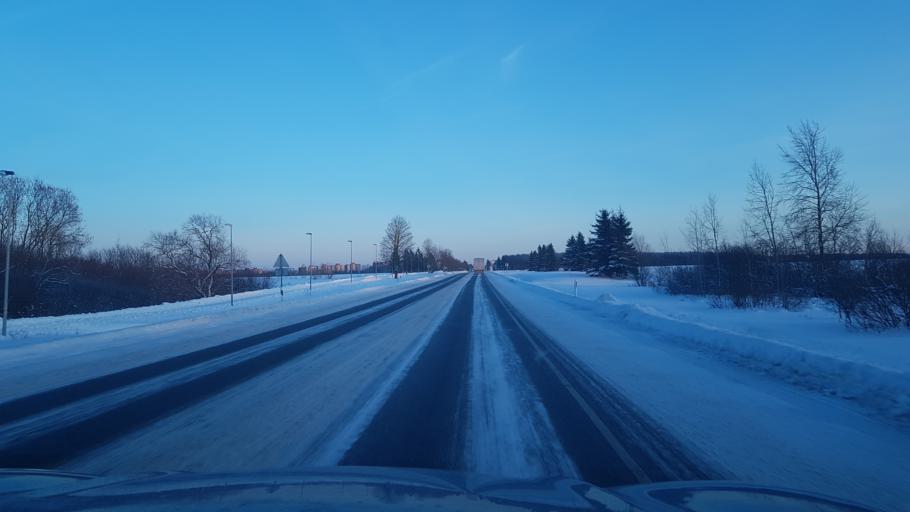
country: EE
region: Ida-Virumaa
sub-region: Narva linn
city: Narva
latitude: 59.3889
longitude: 28.1386
